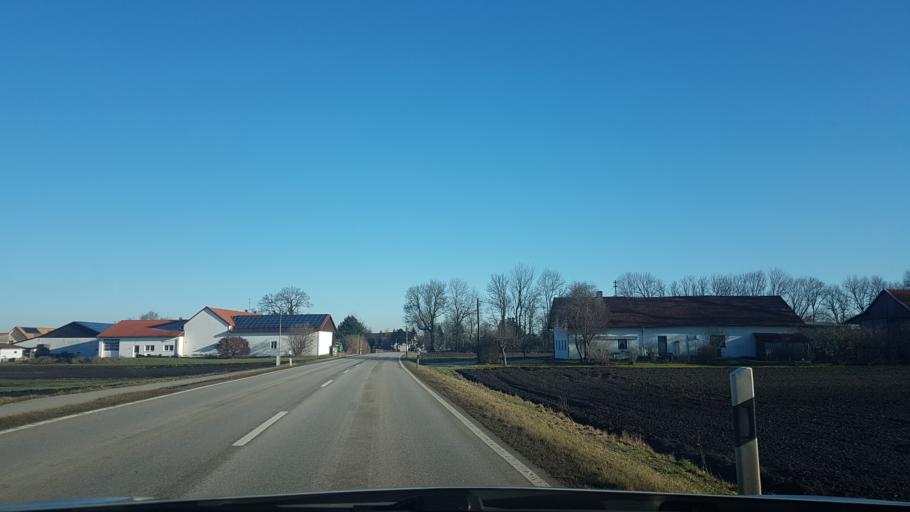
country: DE
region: Bavaria
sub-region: Upper Bavaria
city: Hallbergmoos
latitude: 48.3141
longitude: 11.7847
